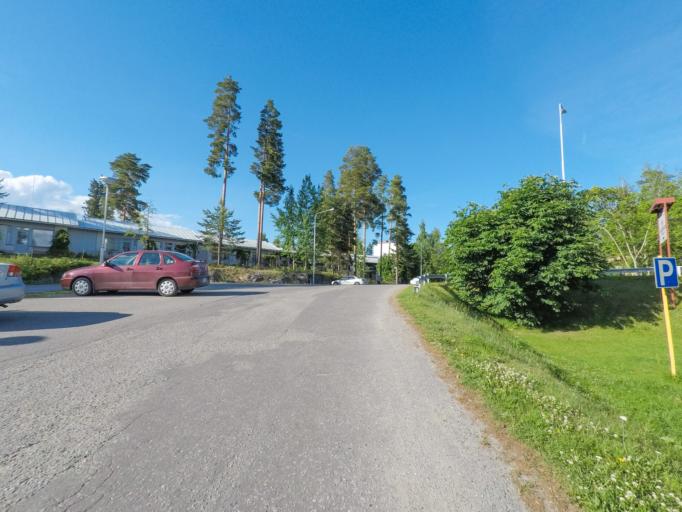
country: FI
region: Southern Savonia
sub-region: Savonlinna
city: Savonlinna
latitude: 61.8720
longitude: 28.8502
